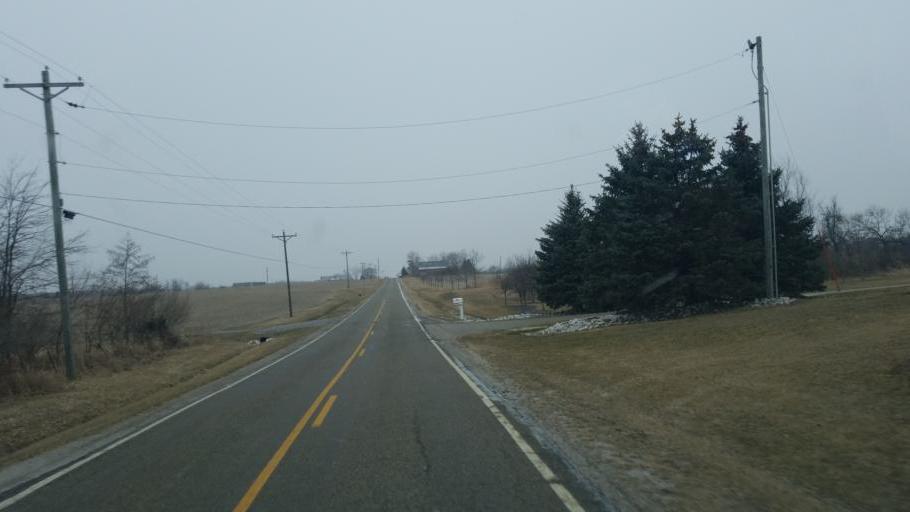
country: US
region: Ohio
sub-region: Defiance County
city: Hicksville
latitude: 41.3249
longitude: -84.7603
